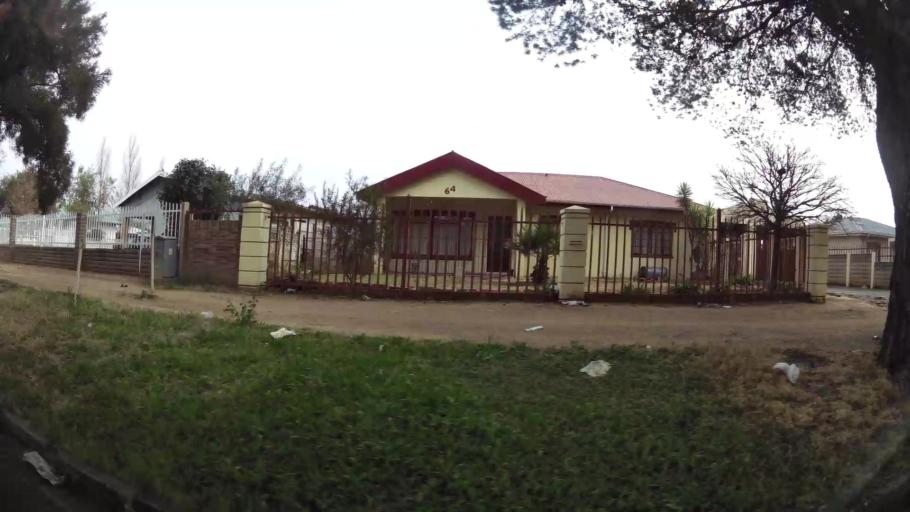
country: ZA
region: Orange Free State
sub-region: Mangaung Metropolitan Municipality
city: Bloemfontein
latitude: -29.1287
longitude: 26.2016
